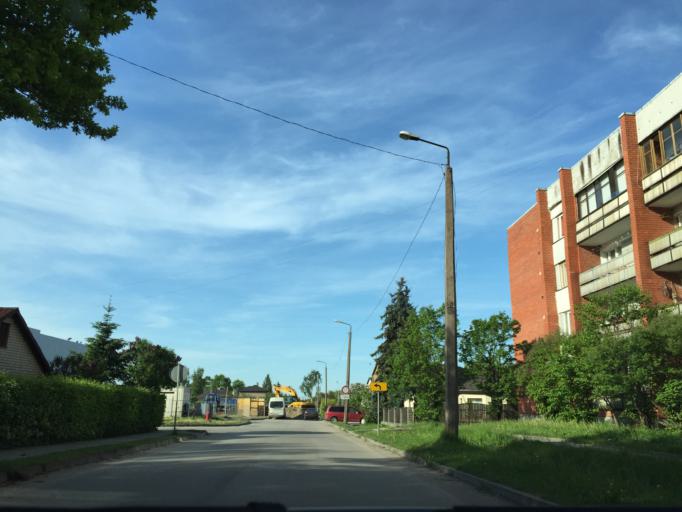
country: LV
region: Jelgava
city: Jelgava
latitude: 56.6358
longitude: 23.7058
